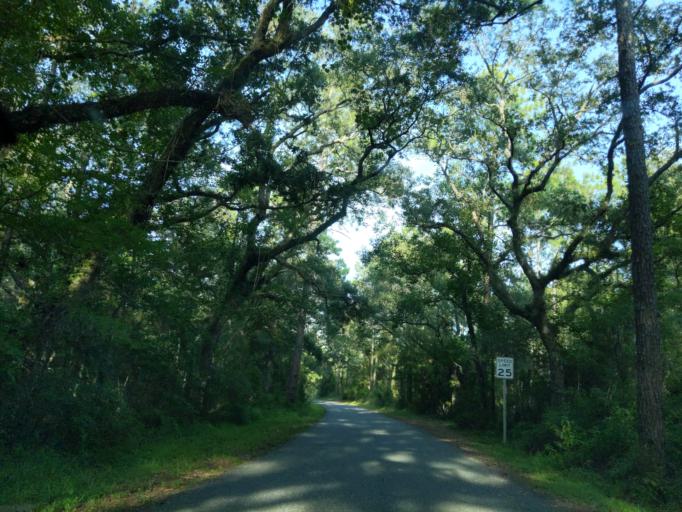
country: US
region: Florida
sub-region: Leon County
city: Tallahassee
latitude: 30.3449
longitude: -84.3841
